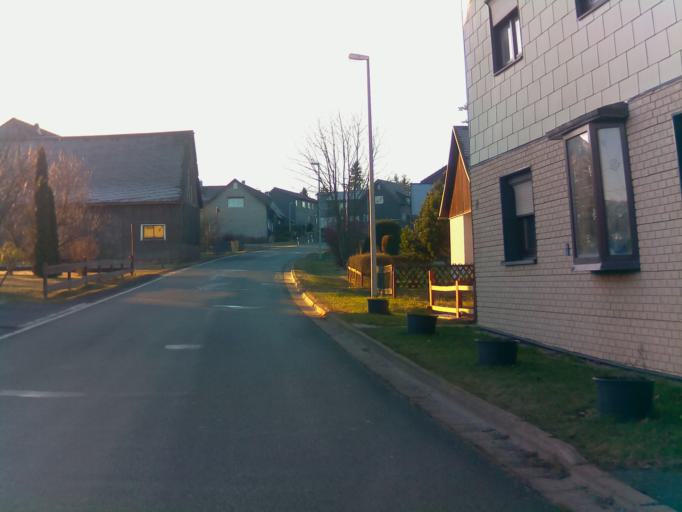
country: DE
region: Thuringia
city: Judenbach
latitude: 50.4321
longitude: 11.2396
